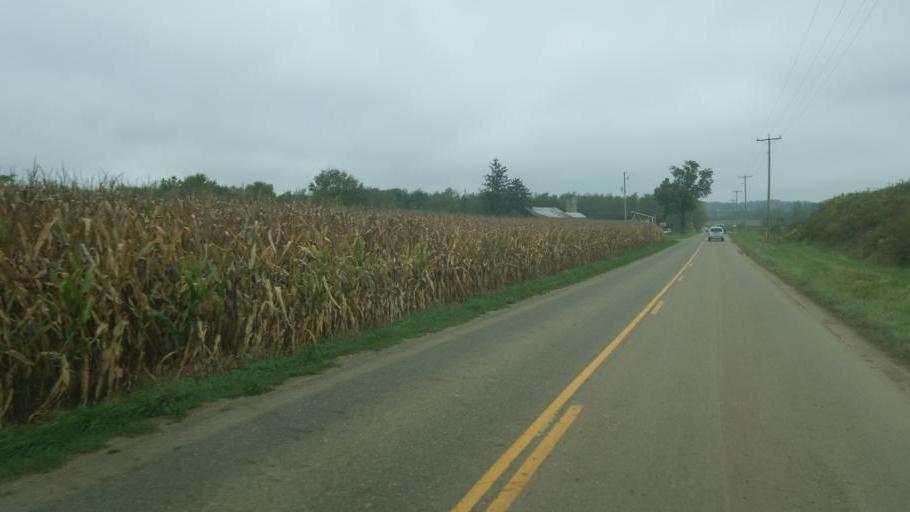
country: US
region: Ohio
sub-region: Tuscarawas County
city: Dover
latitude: 40.6344
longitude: -81.3860
